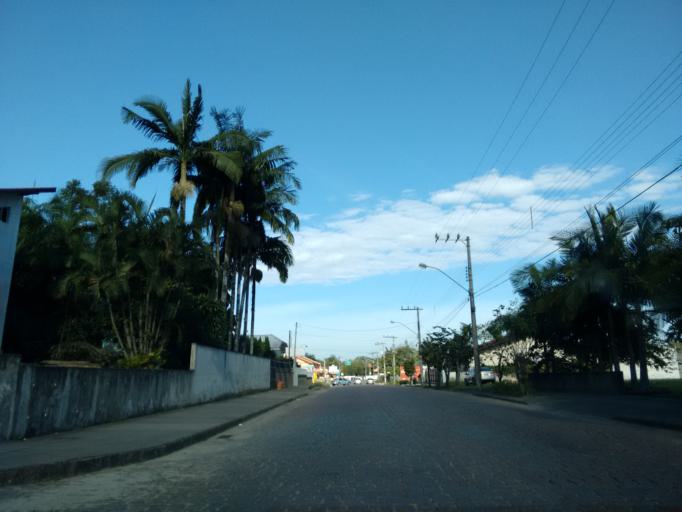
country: BR
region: Santa Catarina
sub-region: Timbo
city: Timbo
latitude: -26.8334
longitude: -49.2667
